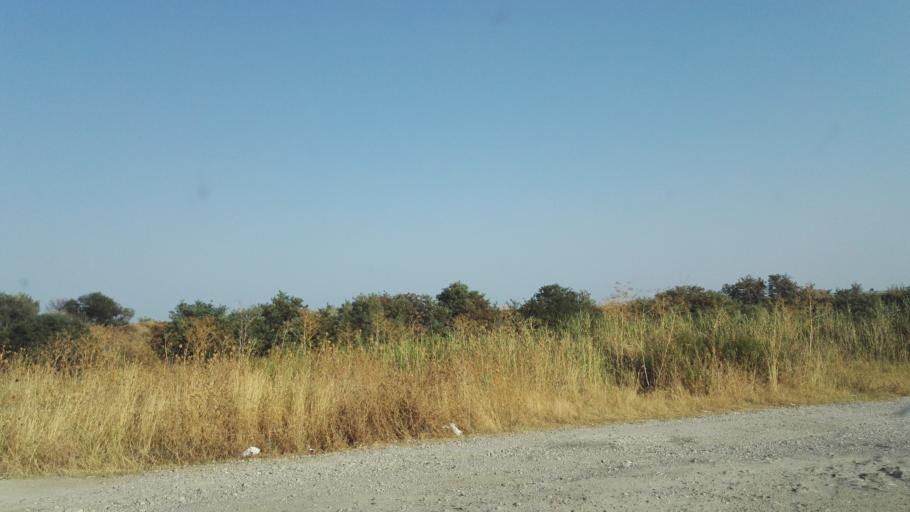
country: IT
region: Calabria
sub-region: Provincia di Reggio Calabria
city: Riace Marina
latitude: 38.3723
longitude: 16.5067
